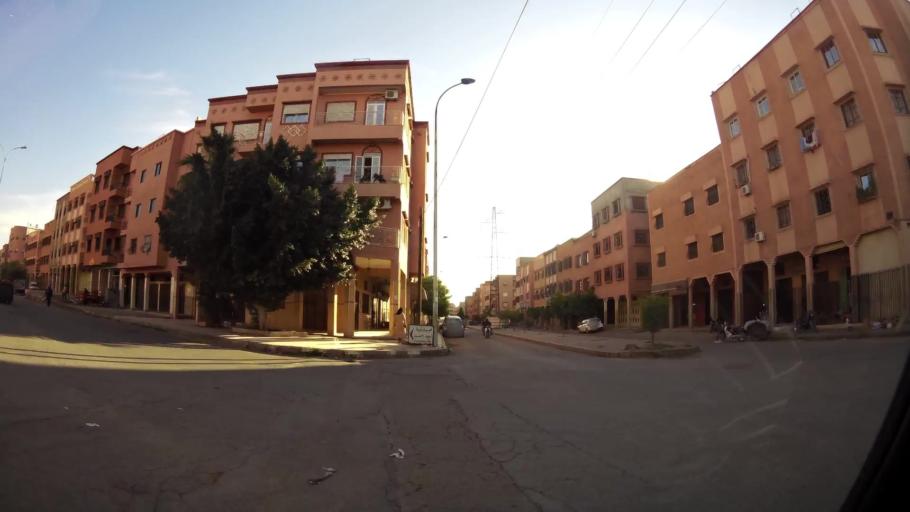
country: MA
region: Marrakech-Tensift-Al Haouz
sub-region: Marrakech
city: Marrakesh
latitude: 31.6166
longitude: -8.0587
